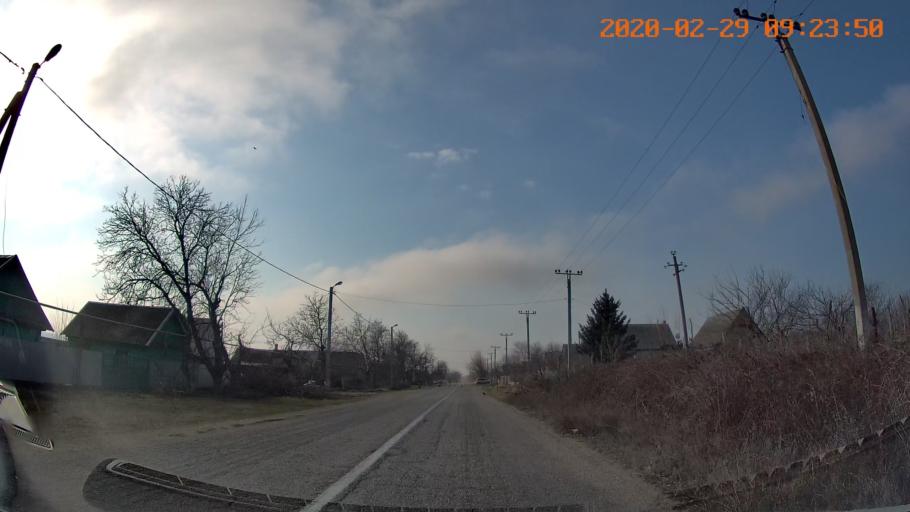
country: MD
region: Telenesti
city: Pervomaisc
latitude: 46.7219
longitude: 29.9602
